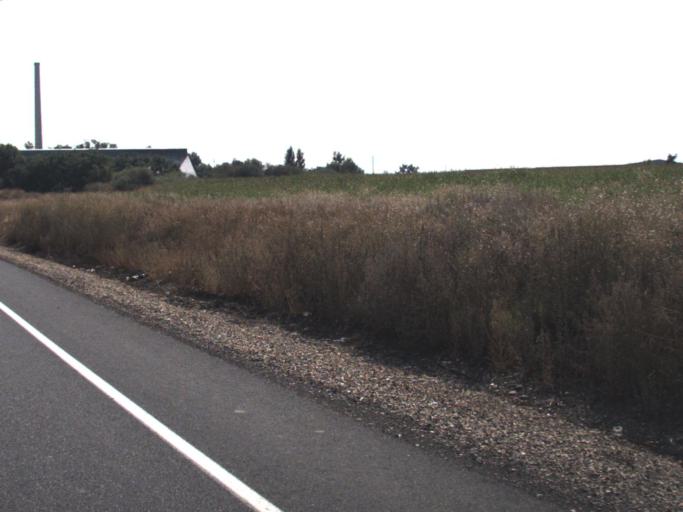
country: US
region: Washington
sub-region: Yakima County
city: Toppenish
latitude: 46.3993
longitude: -120.3145
